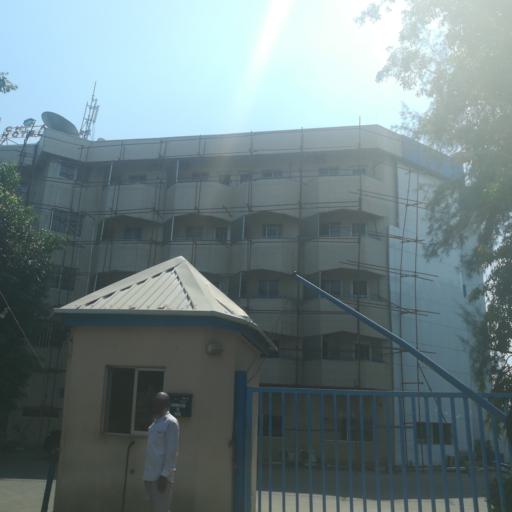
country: NG
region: Abuja Federal Capital Territory
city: Abuja
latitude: 9.0721
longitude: 7.4343
